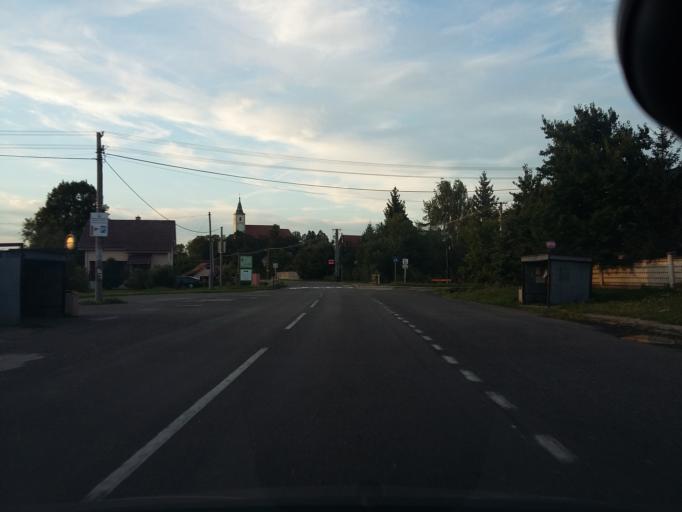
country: SK
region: Bratislavsky
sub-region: Okres Malacky
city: Malacky
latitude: 48.4033
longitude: 17.1551
